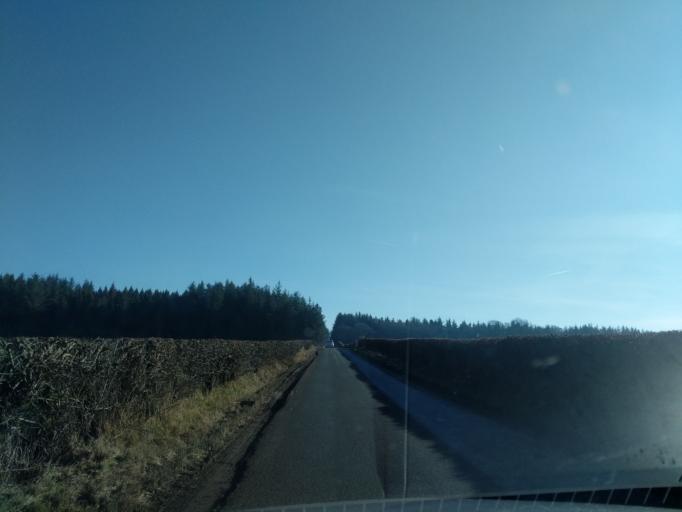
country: GB
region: Scotland
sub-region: South Lanarkshire
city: Carluke
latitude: 55.6946
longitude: -3.8489
